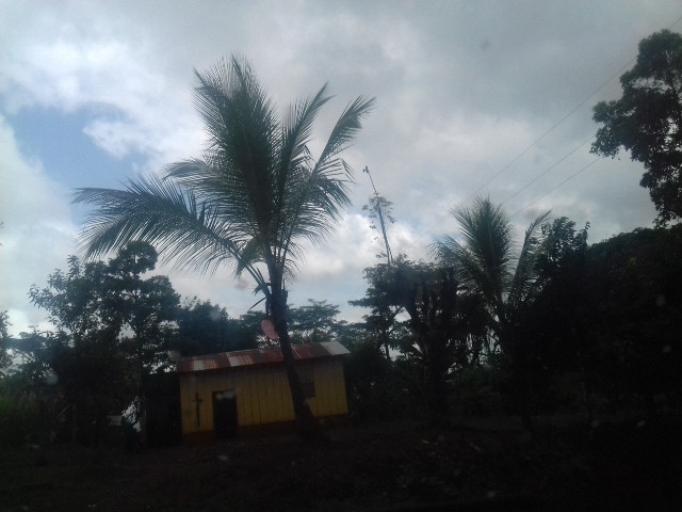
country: NI
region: Matagalpa
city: Matiguas
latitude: 12.9375
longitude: -85.3687
